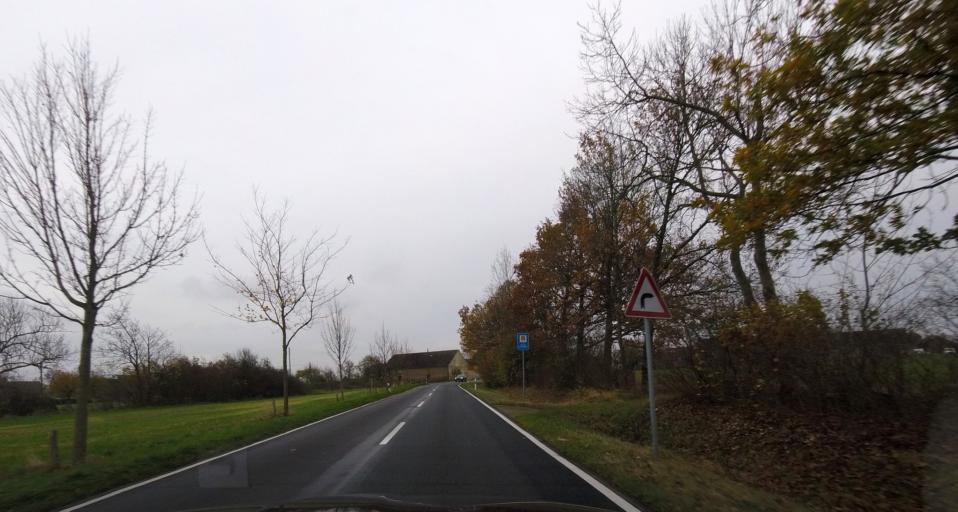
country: DE
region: Brandenburg
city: Niemegk
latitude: 52.0295
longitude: 12.7369
